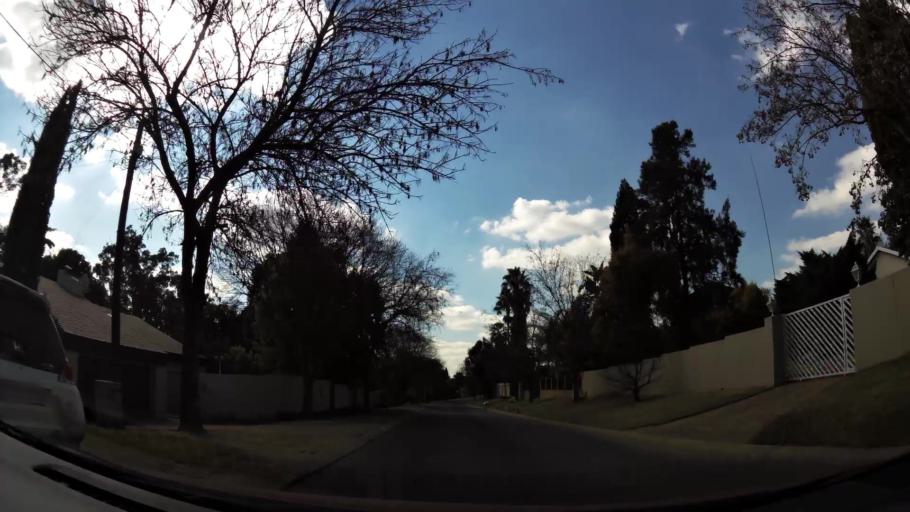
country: ZA
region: Gauteng
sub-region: City of Johannesburg Metropolitan Municipality
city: Roodepoort
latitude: -26.0741
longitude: 27.9494
